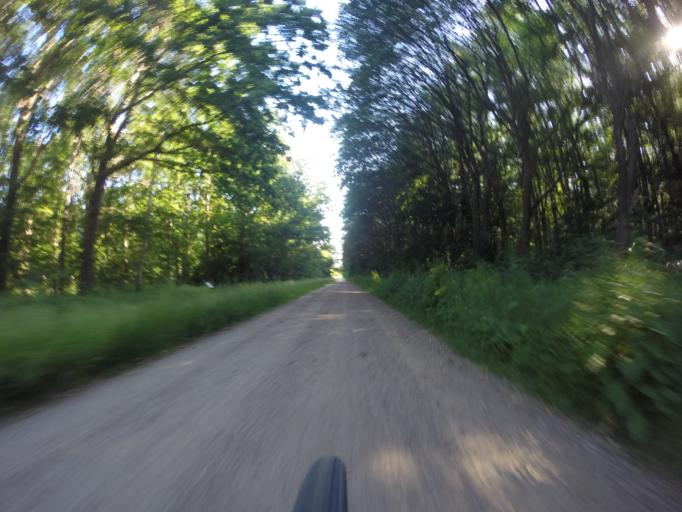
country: DK
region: Capital Region
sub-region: Albertslund Kommune
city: Albertslund
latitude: 55.6916
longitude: 12.3277
